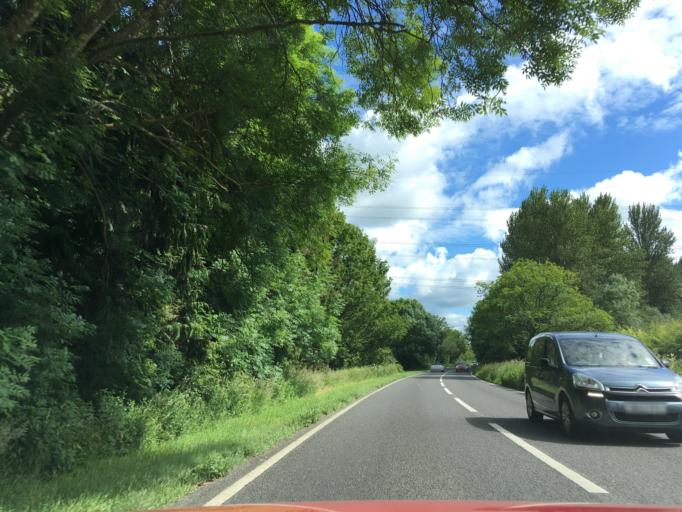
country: GB
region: England
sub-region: Gloucestershire
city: Lechlade
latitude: 51.7261
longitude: -1.6734
